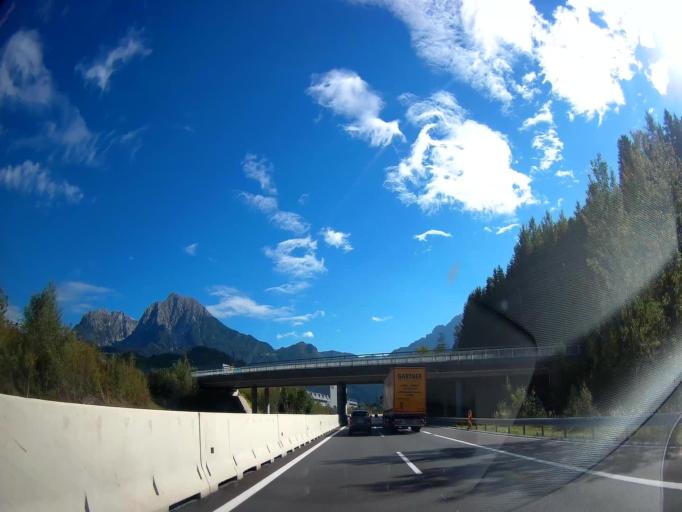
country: AT
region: Upper Austria
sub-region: Politischer Bezirk Kirchdorf an der Krems
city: Rossleithen
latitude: 47.6856
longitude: 14.3223
